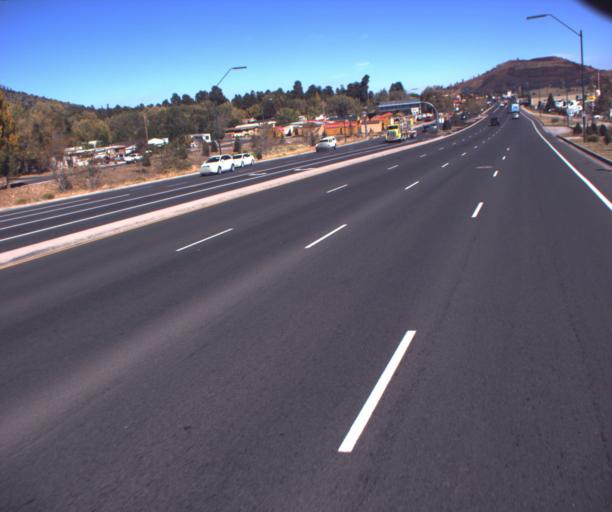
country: US
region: Arizona
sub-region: Coconino County
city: Flagstaff
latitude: 35.2214
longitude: -111.5875
